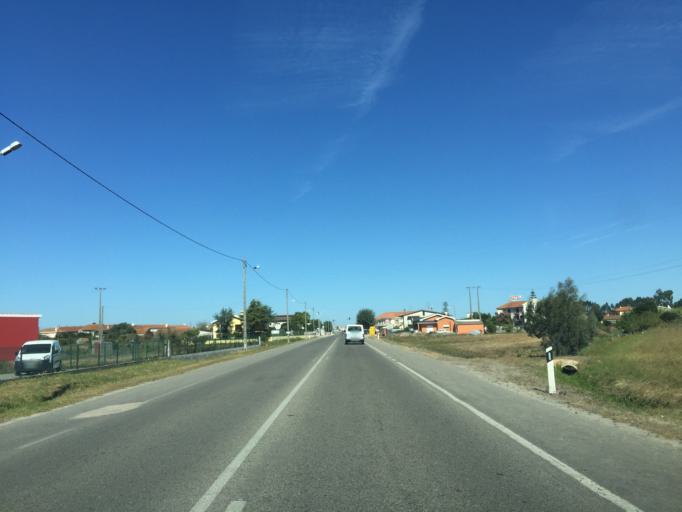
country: PT
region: Coimbra
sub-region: Montemor-O-Velho
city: Arazede
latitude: 40.3040
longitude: -8.7585
